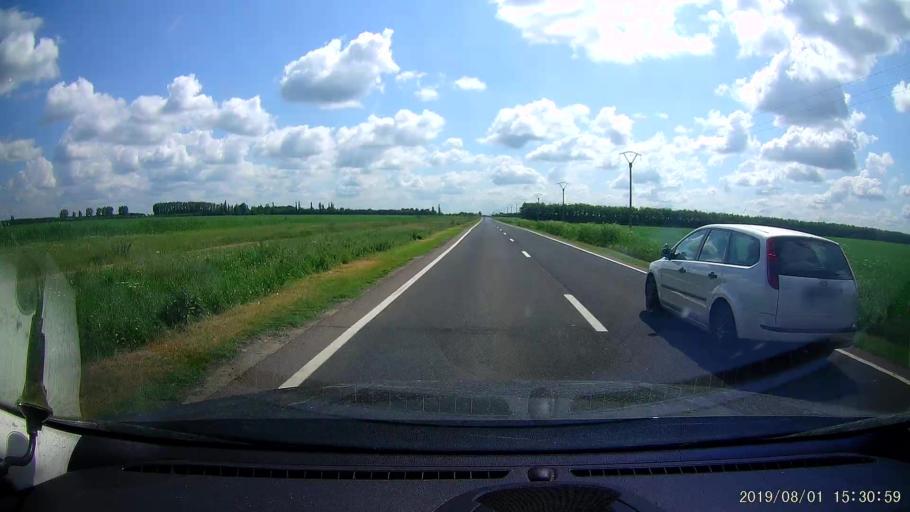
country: RO
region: Braila
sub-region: Comuna Stancuta
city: Cuza Voda
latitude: 44.9530
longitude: 27.6666
